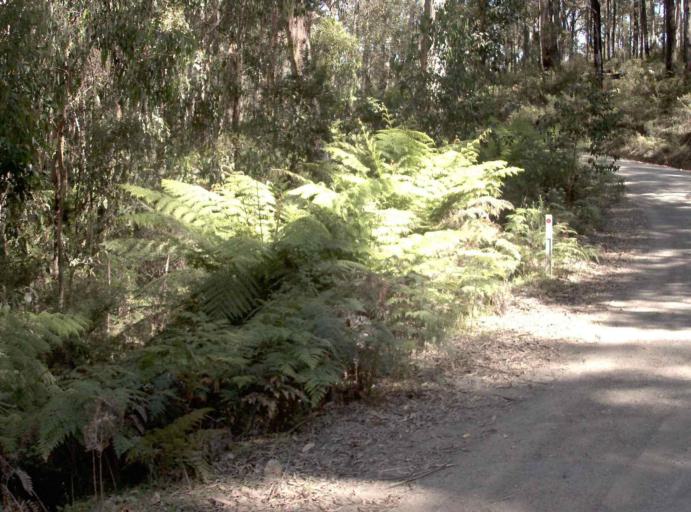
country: AU
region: New South Wales
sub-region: Bombala
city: Bombala
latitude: -37.2617
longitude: 148.7300
